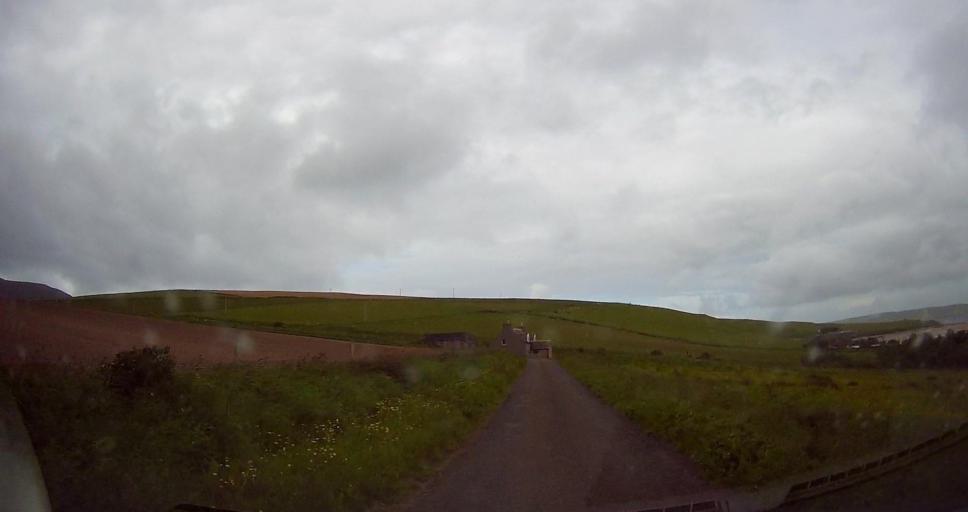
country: GB
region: Scotland
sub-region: Orkney Islands
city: Stromness
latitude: 58.9150
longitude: -3.3254
